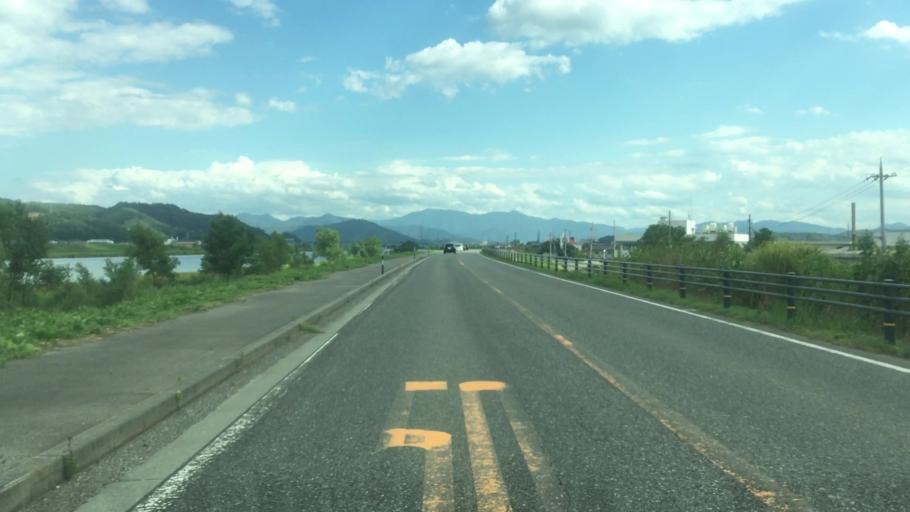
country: JP
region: Hyogo
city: Toyooka
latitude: 35.5727
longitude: 134.8072
